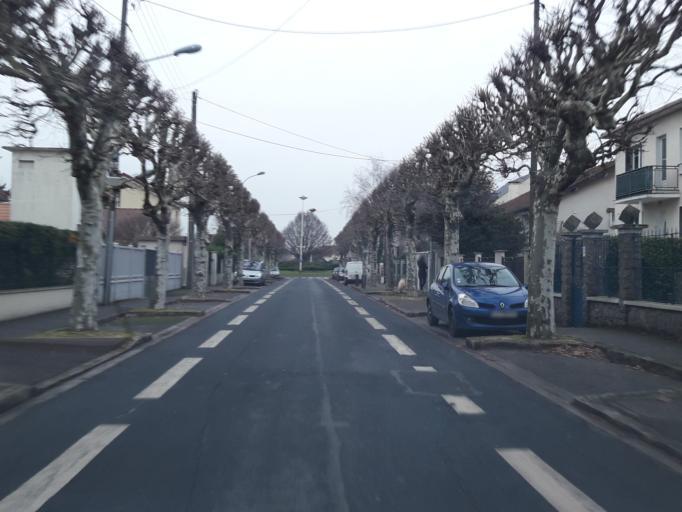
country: FR
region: Ile-de-France
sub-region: Departement de l'Essonne
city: Morsang-sur-Orge
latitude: 48.6500
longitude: 2.3505
